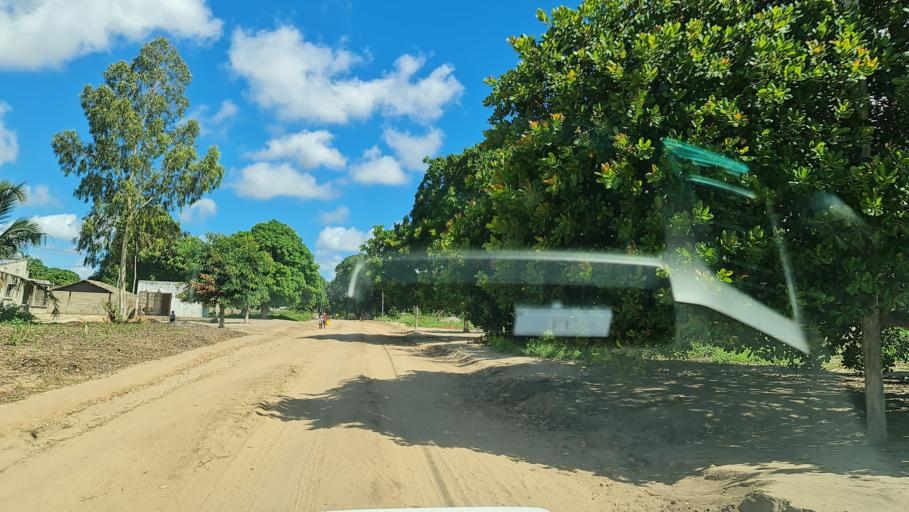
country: MZ
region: Nampula
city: Ilha de Mocambique
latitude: -15.5502
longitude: 40.4063
